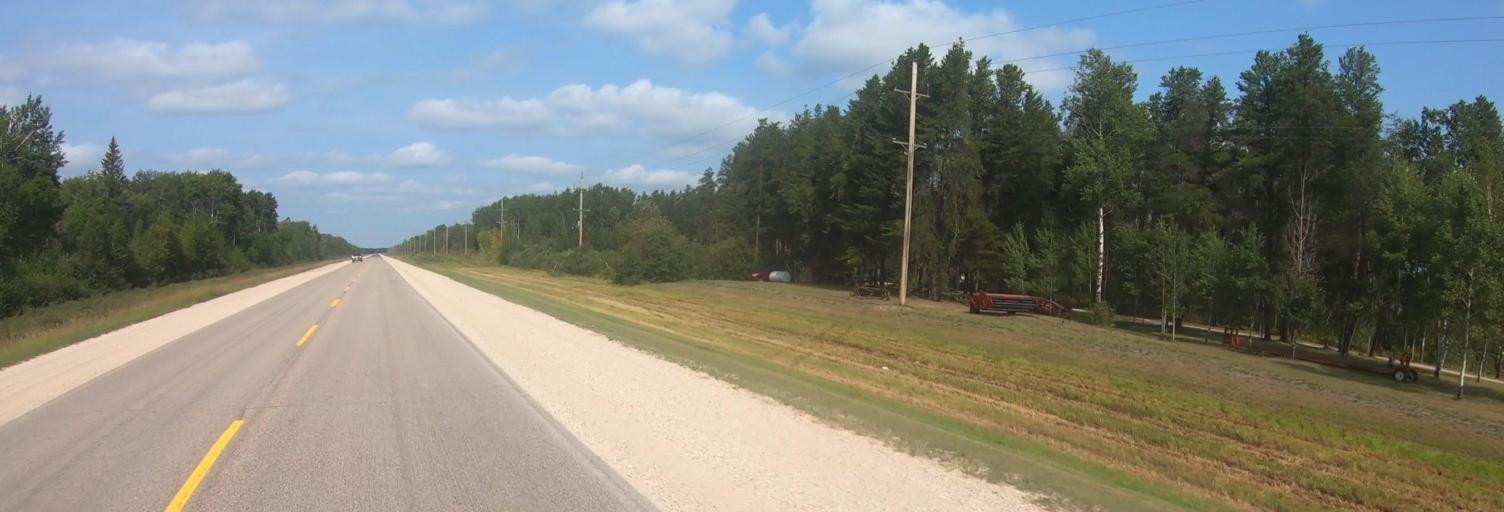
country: CA
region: Manitoba
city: La Broquerie
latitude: 49.2255
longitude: -96.3159
